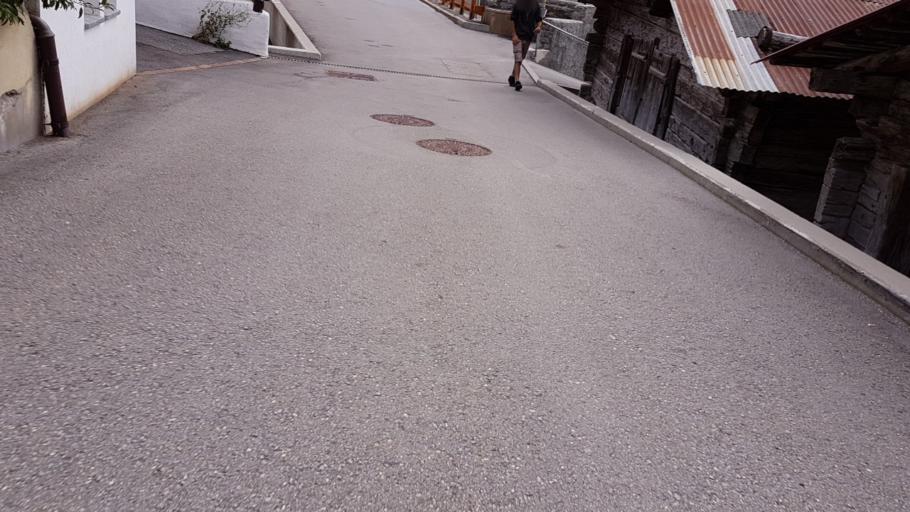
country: CH
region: Valais
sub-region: Leuk District
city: Leukerbad
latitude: 46.3807
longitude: 7.6285
